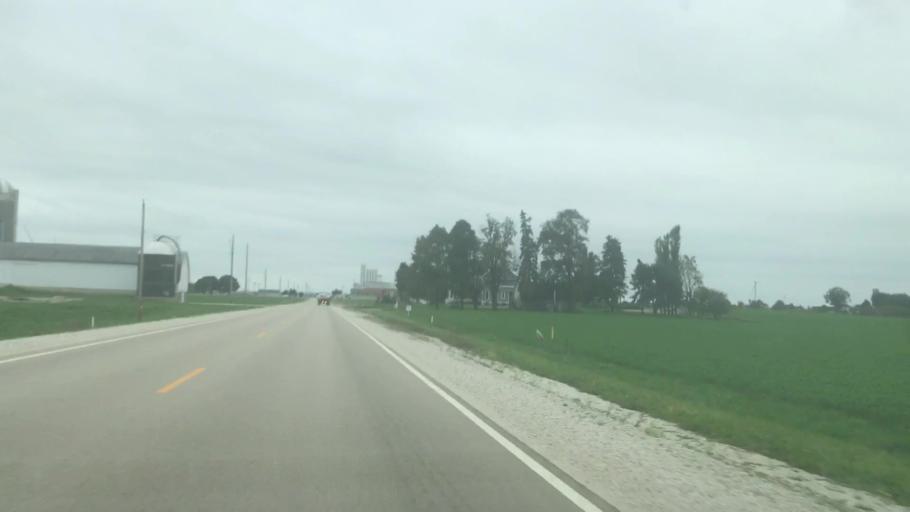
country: US
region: Wisconsin
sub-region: Fond du Lac County
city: Oakfield
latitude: 43.6222
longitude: -88.5417
